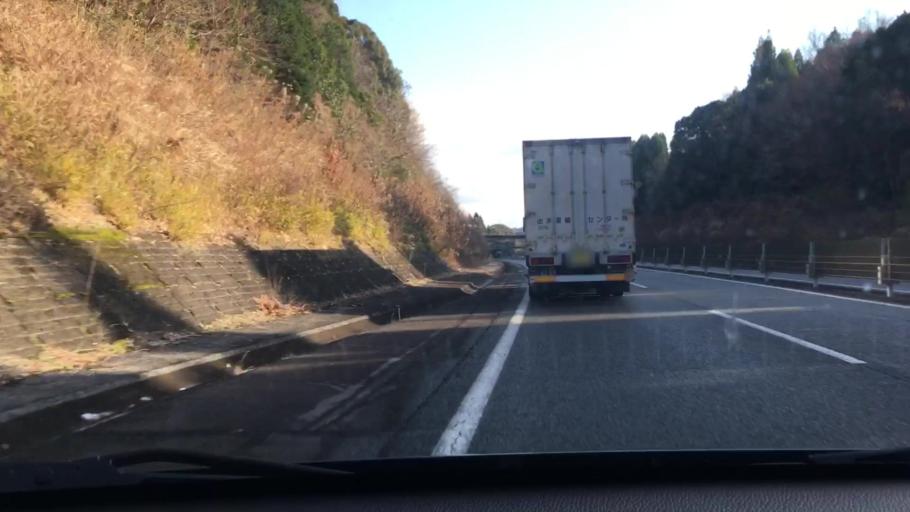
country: JP
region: Kagoshima
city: Okuchi-shinohara
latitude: 31.9125
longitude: 130.7043
